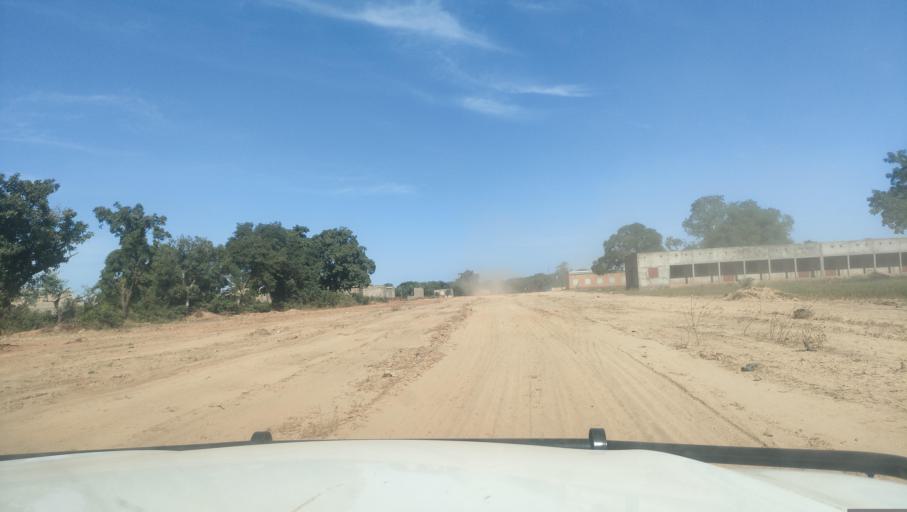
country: BF
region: Est
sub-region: Province du Gourma
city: Fada N'gourma
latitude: 12.0699
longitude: 0.3352
